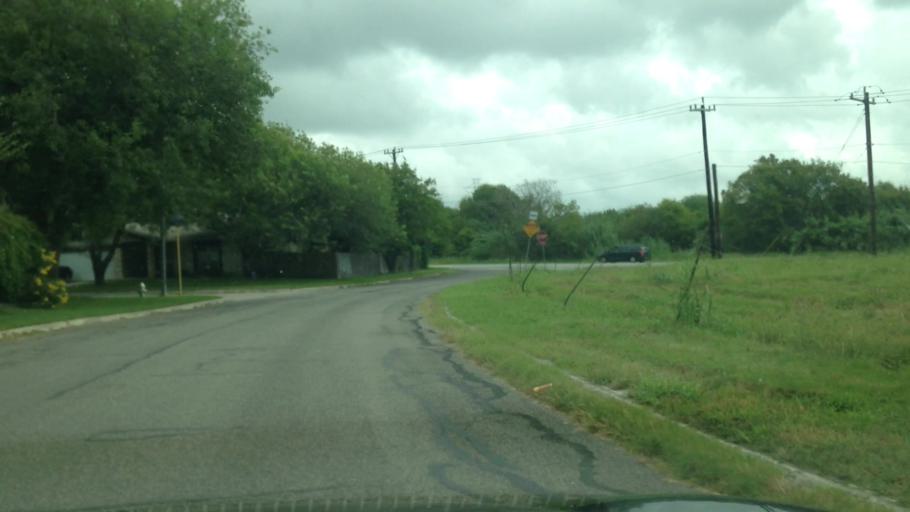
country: US
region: Texas
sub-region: Bexar County
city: Live Oak
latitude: 29.5807
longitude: -98.4036
